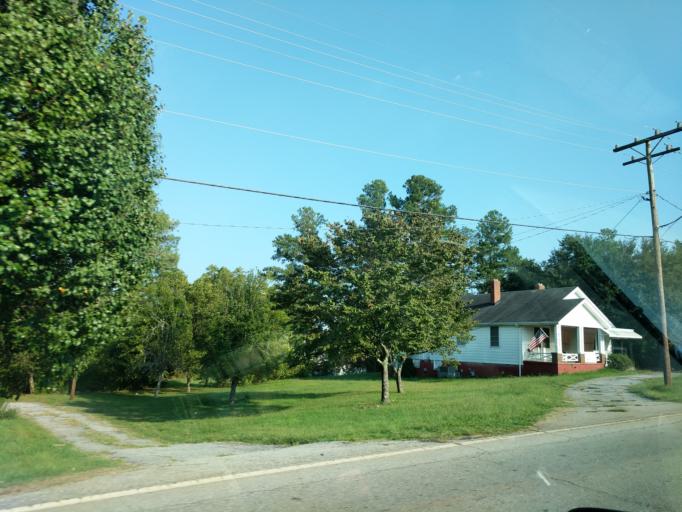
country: US
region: South Carolina
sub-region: Anderson County
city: Piedmont
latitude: 34.7046
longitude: -82.4534
